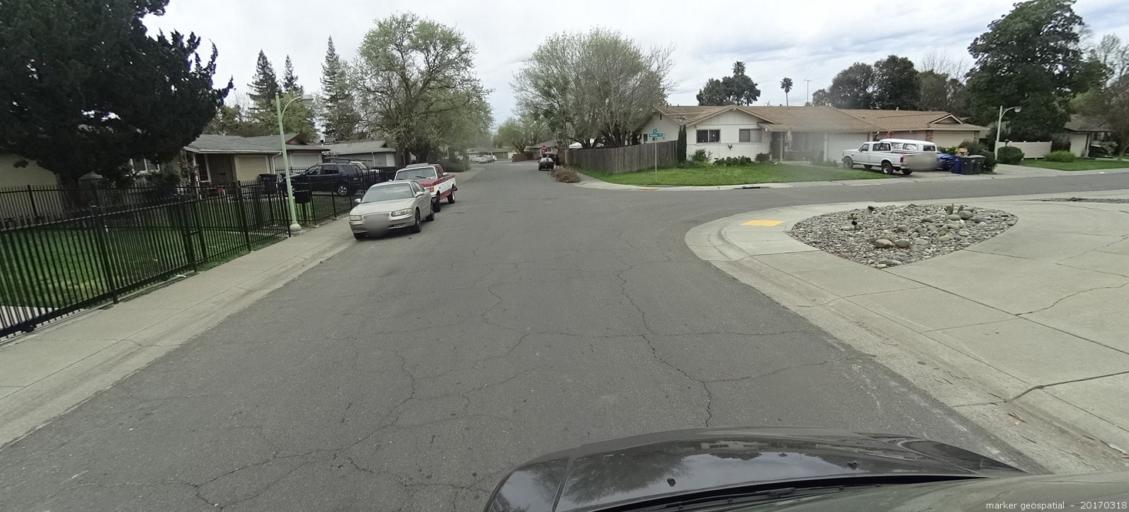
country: US
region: California
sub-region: Sacramento County
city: Parkway
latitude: 38.4832
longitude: -121.4493
